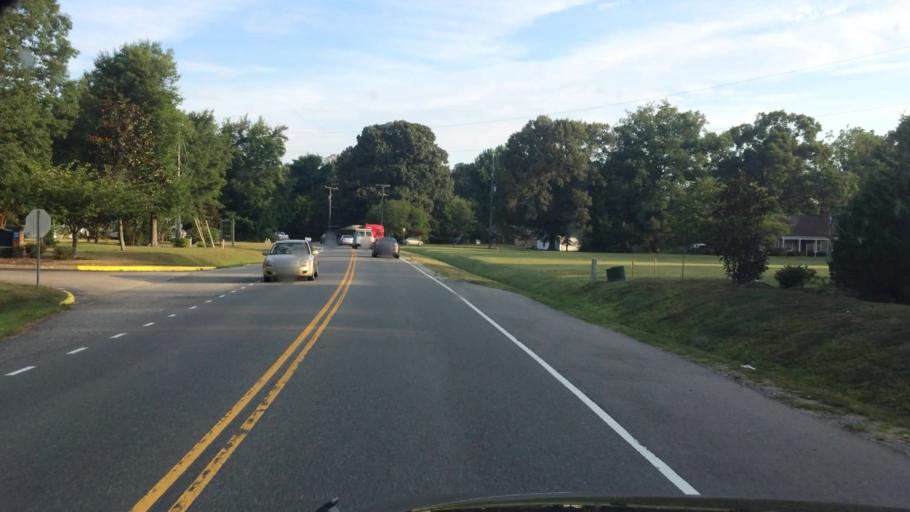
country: US
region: Virginia
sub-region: James City County
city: Williamsburg
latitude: 37.3158
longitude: -76.7310
